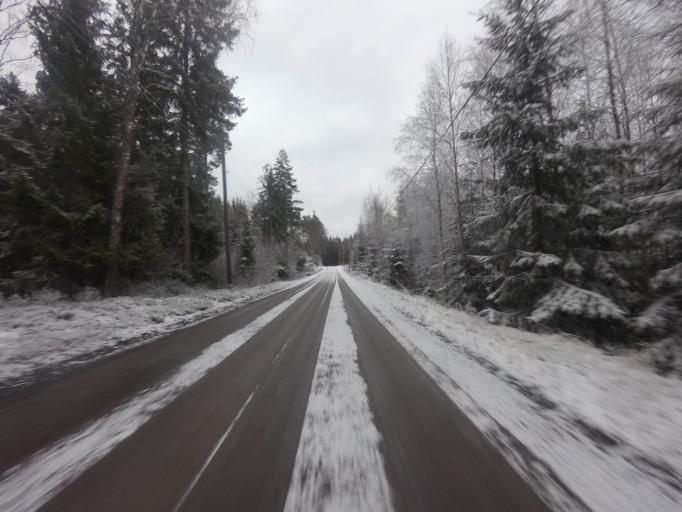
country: SE
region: Skane
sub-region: Osby Kommun
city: Lonsboda
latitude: 56.3911
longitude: 14.2777
